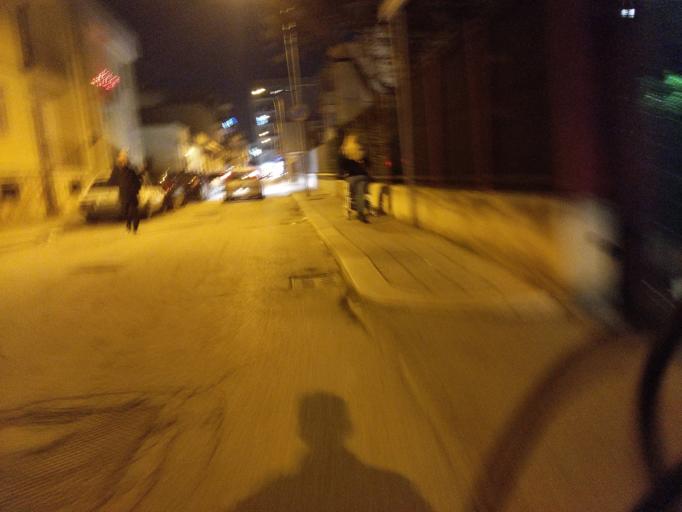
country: IT
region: Apulia
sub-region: Provincia di Bari
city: Modugno
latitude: 41.0856
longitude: 16.7883
